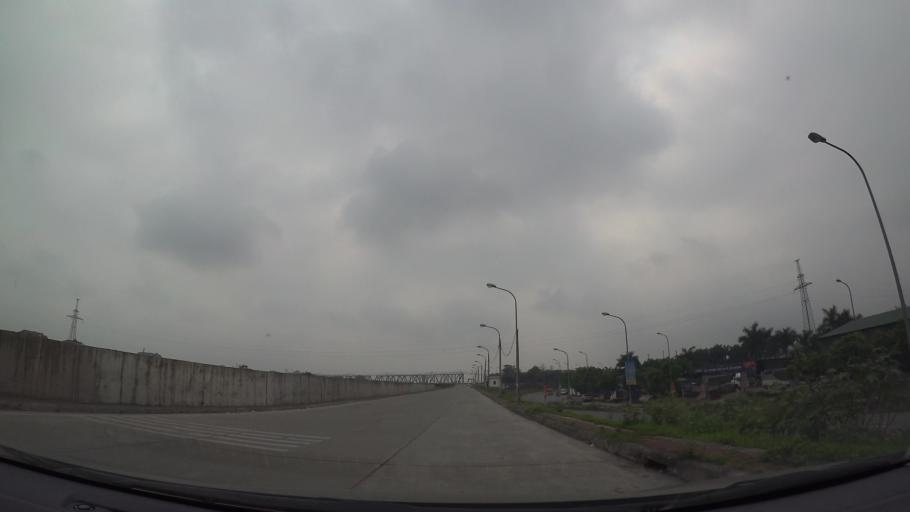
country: VN
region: Ha Noi
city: Trau Quy
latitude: 21.0770
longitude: 105.9044
